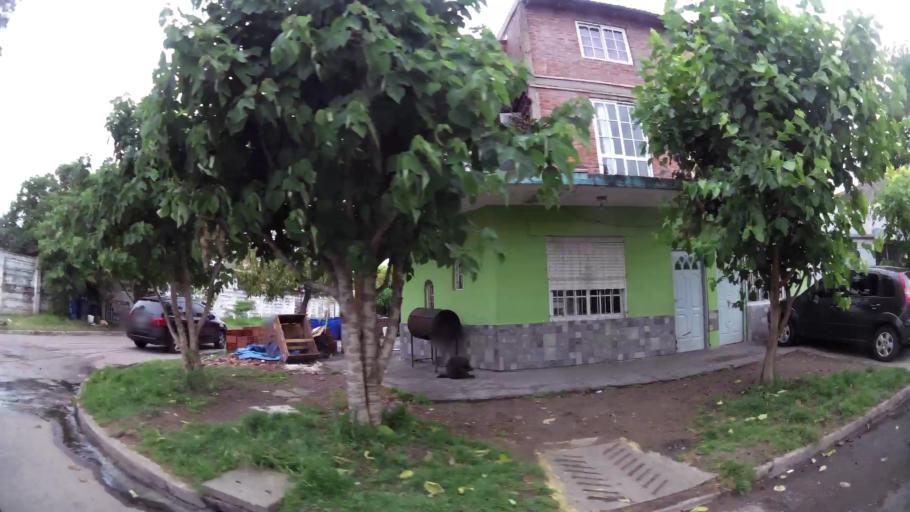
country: AR
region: Buenos Aires
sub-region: Partido de Lanus
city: Lanus
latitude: -34.7356
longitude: -58.3598
